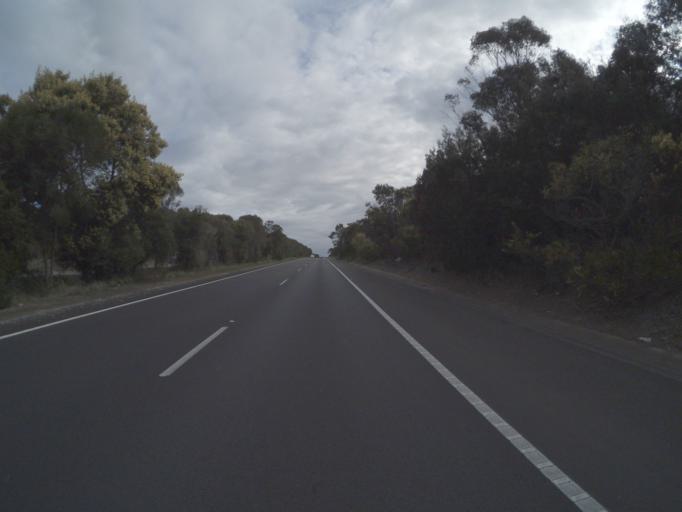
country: AU
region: New South Wales
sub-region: Wingecarribee
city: Bundanoon
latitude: -34.5978
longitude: 150.2387
